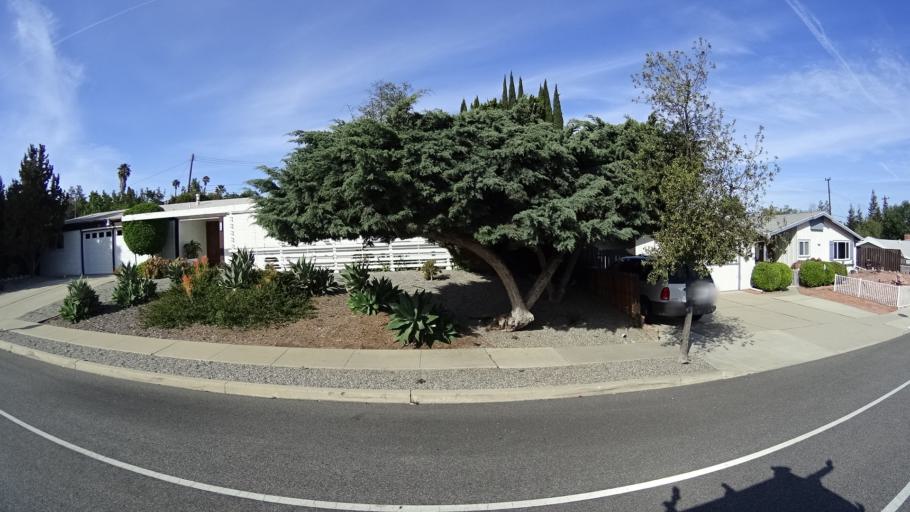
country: US
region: California
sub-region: Ventura County
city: Thousand Oaks
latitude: 34.1922
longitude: -118.8693
